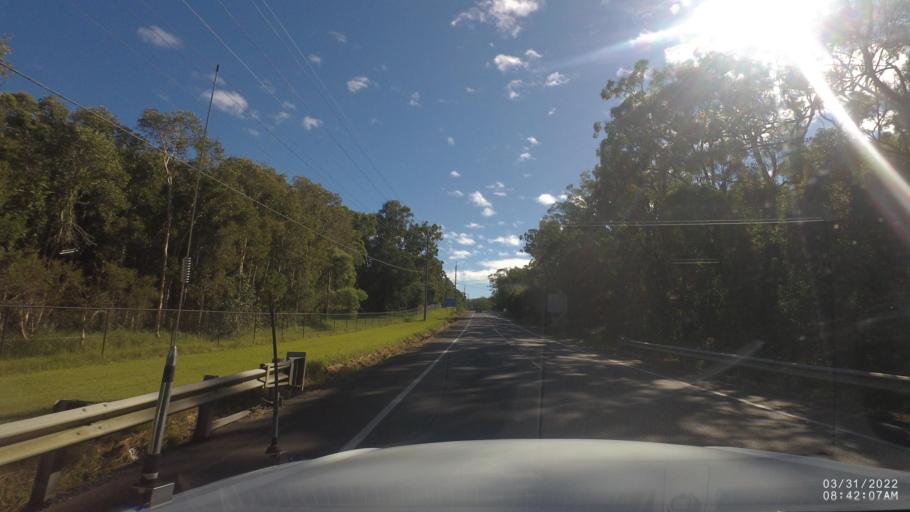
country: AU
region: Queensland
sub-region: Gold Coast
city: Yatala
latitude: -27.6569
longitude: 153.2356
